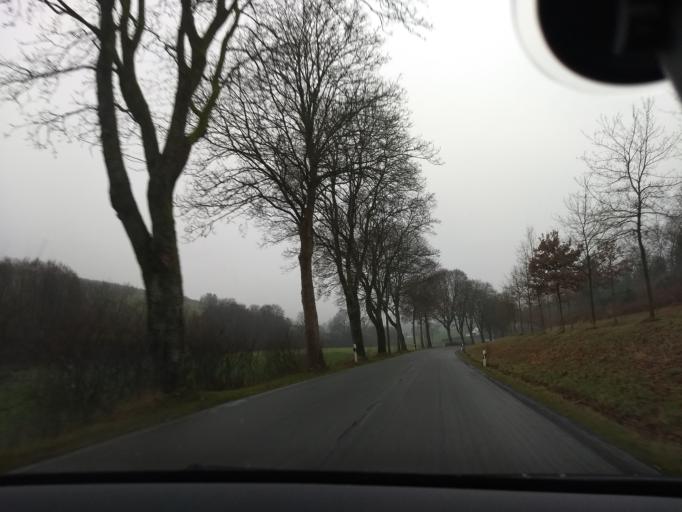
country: DE
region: North Rhine-Westphalia
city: Eslohe
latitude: 51.2422
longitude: 8.1387
